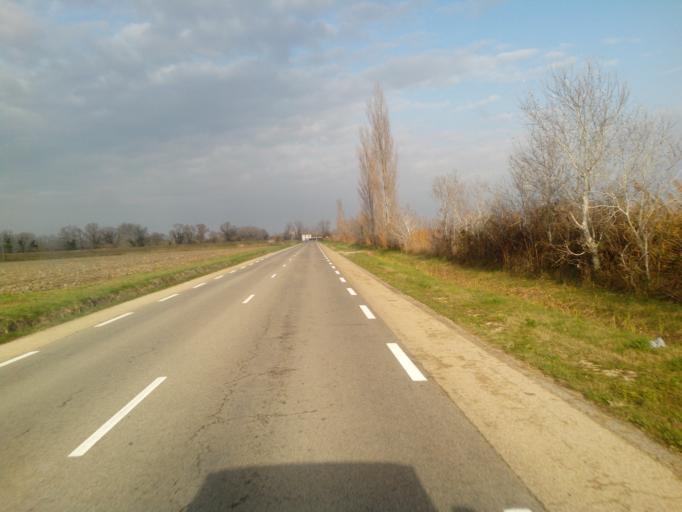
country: FR
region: Languedoc-Roussillon
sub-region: Departement du Gard
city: Saint-Gilles
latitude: 43.5986
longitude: 4.4725
